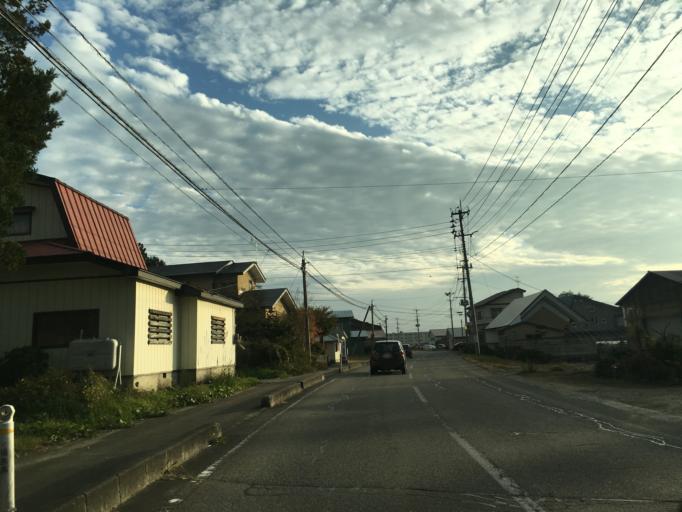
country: JP
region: Fukushima
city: Inawashiro
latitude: 37.5459
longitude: 140.1392
